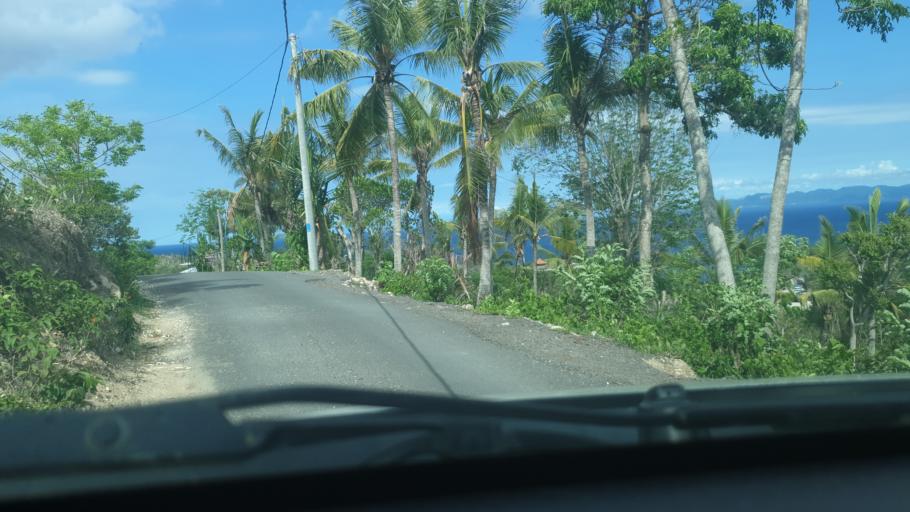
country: ID
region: Bali
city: Tanglad
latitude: -8.7748
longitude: 115.6165
